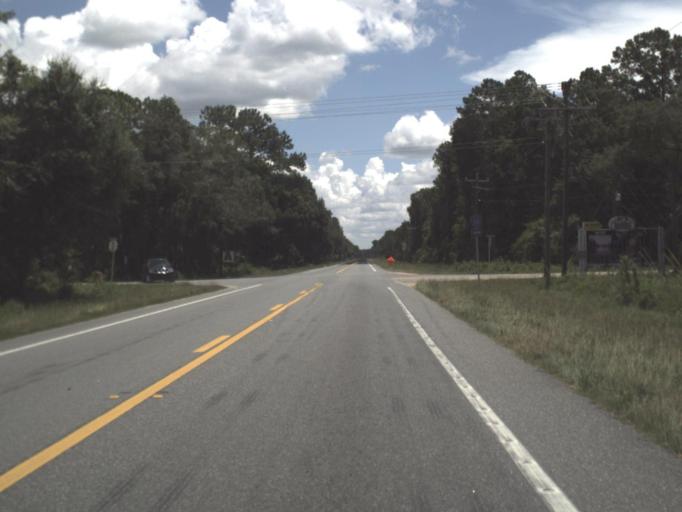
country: US
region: Florida
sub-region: Taylor County
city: Perry
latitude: 30.1411
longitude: -83.9013
